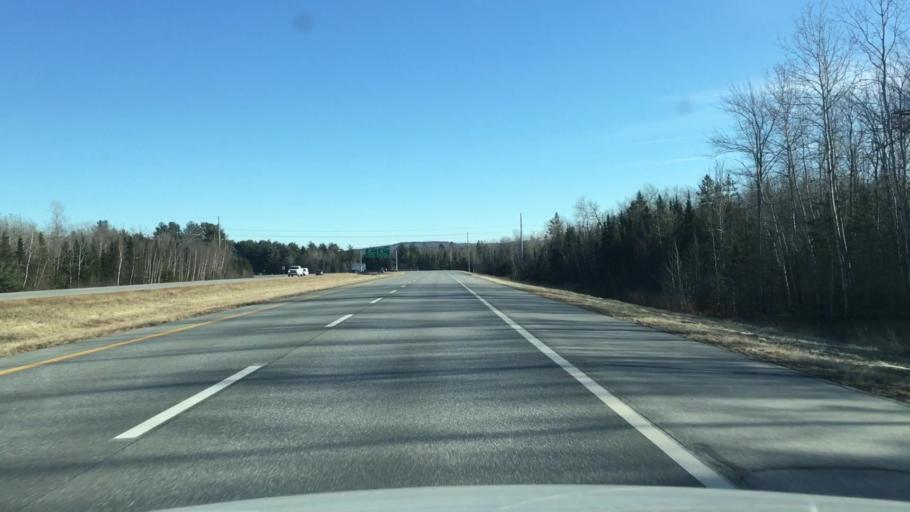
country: US
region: Maine
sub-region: Penobscot County
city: Brewer
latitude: 44.7699
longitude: -68.7385
